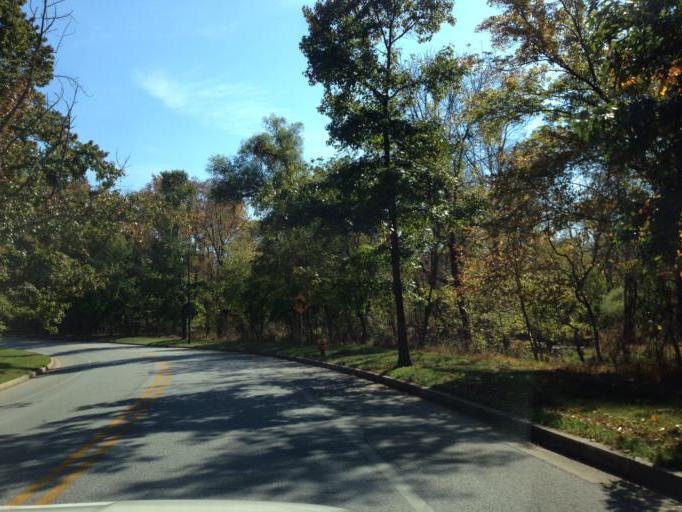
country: US
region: Maryland
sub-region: Howard County
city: Columbia
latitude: 39.2489
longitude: -76.8310
